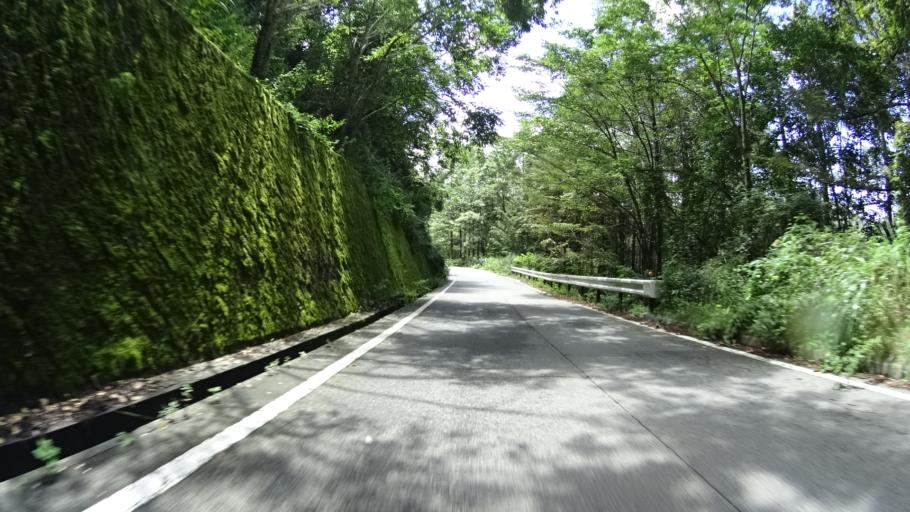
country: JP
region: Yamanashi
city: Enzan
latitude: 35.7153
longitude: 138.8364
